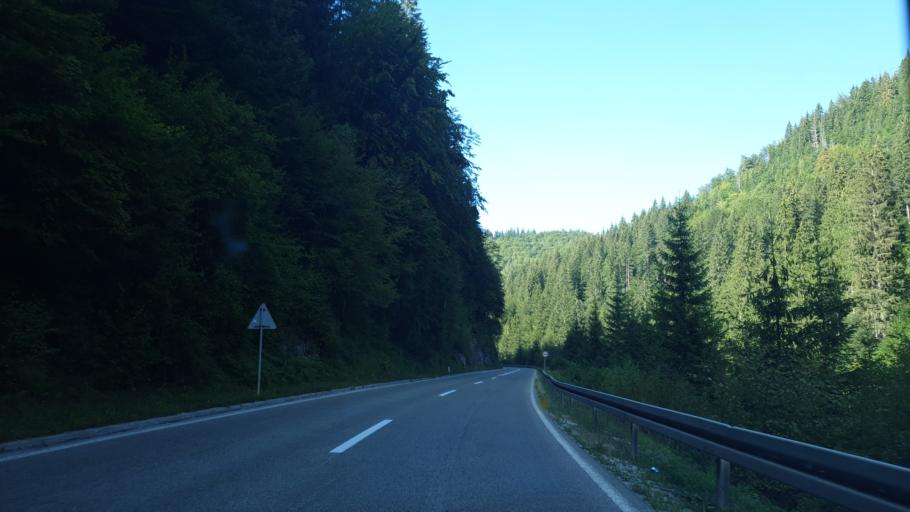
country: RS
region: Central Serbia
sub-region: Zlatiborski Okrug
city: Nova Varos
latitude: 43.4836
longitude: 19.8266
